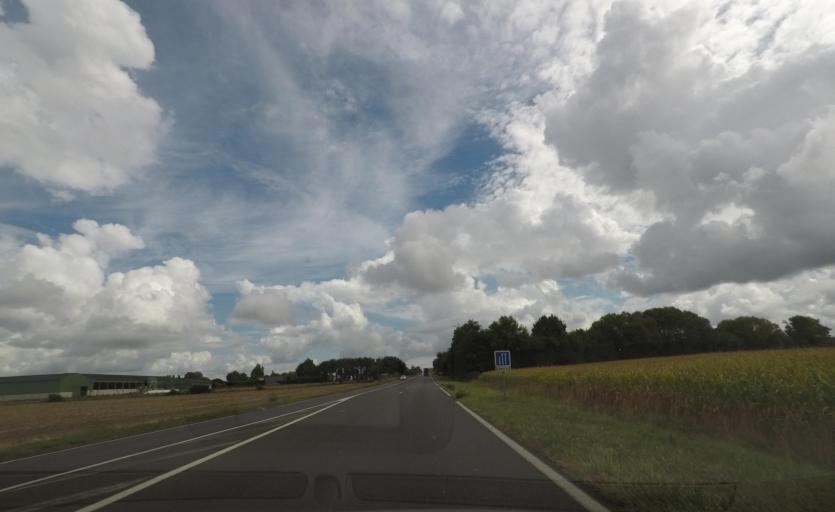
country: FR
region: Pays de la Loire
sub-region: Departement de Maine-et-Loire
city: Corze
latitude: 47.5481
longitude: -0.3917
